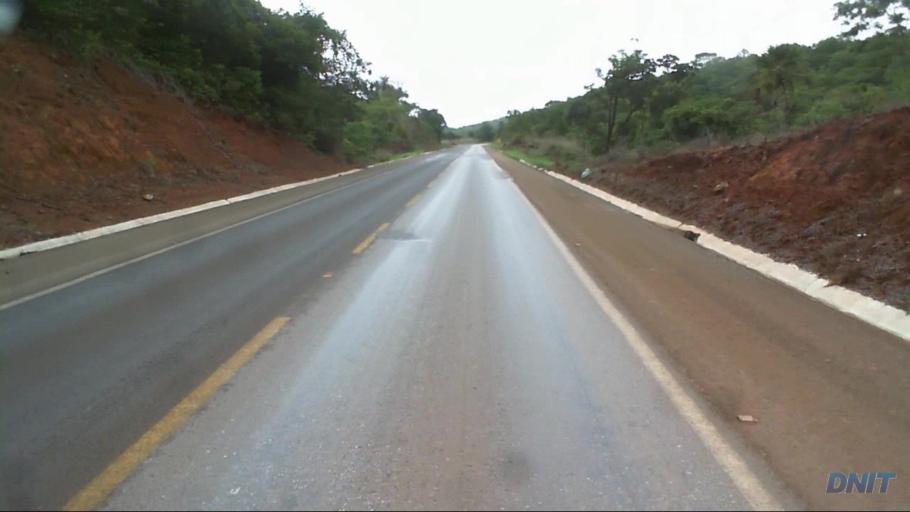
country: BR
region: Goias
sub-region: Barro Alto
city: Barro Alto
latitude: -14.9237
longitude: -48.9501
